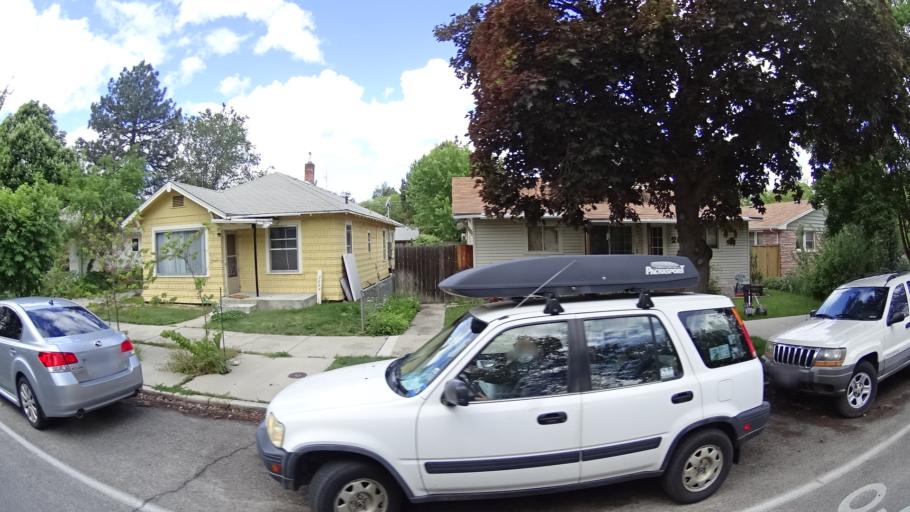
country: US
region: Idaho
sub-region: Ada County
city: Boise
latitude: 43.6361
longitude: -116.2059
